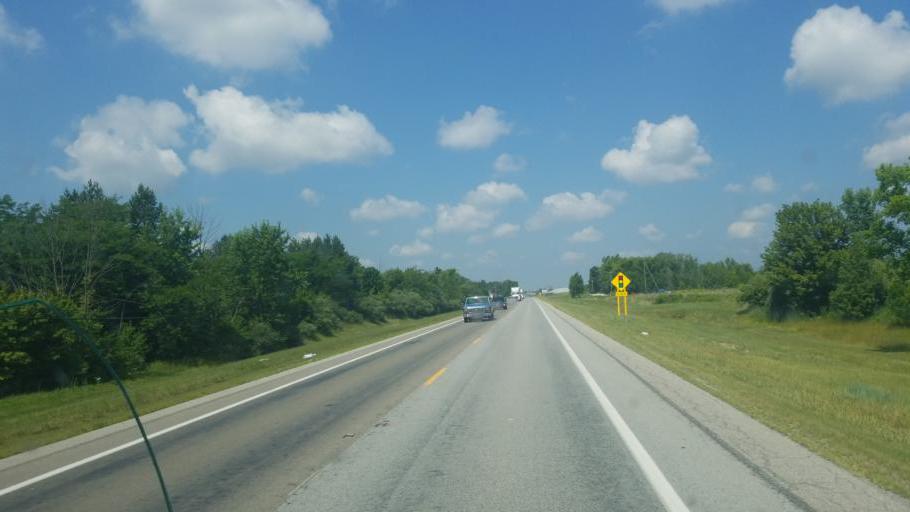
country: US
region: Ohio
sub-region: Allen County
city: Lima
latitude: 40.7198
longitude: -84.0425
